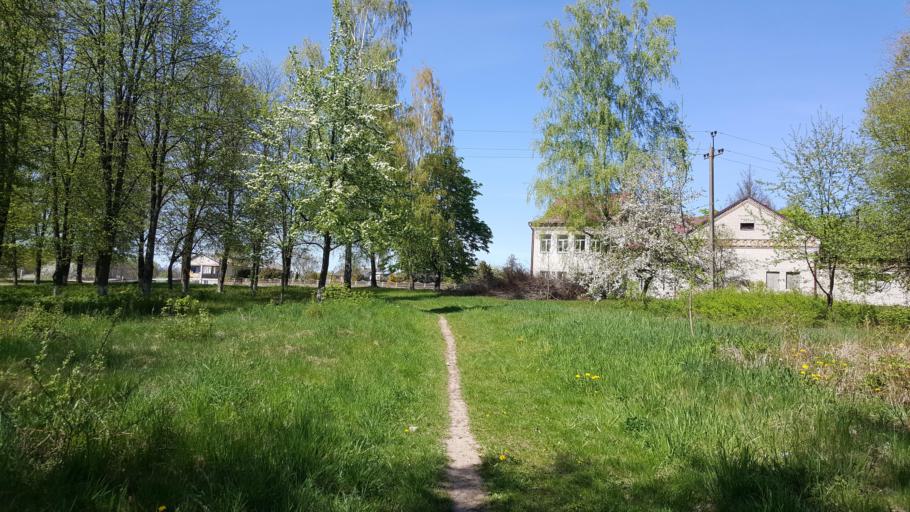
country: BY
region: Brest
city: Kamyanyets
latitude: 52.4399
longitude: 23.8475
